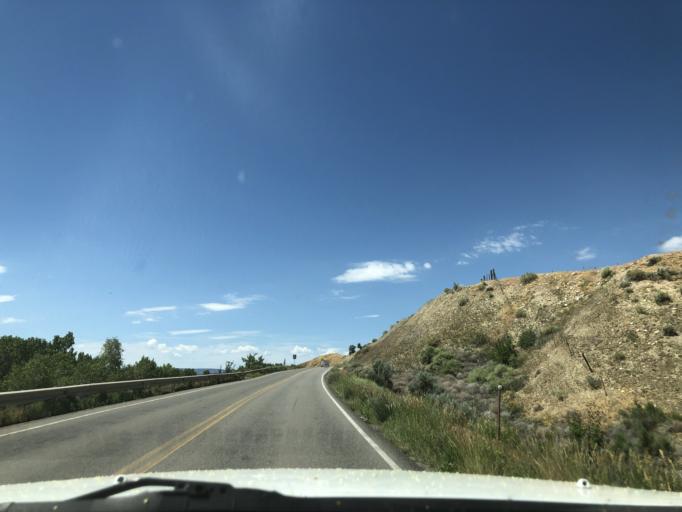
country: US
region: Colorado
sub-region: Delta County
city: Paonia
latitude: 38.8214
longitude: -107.6897
